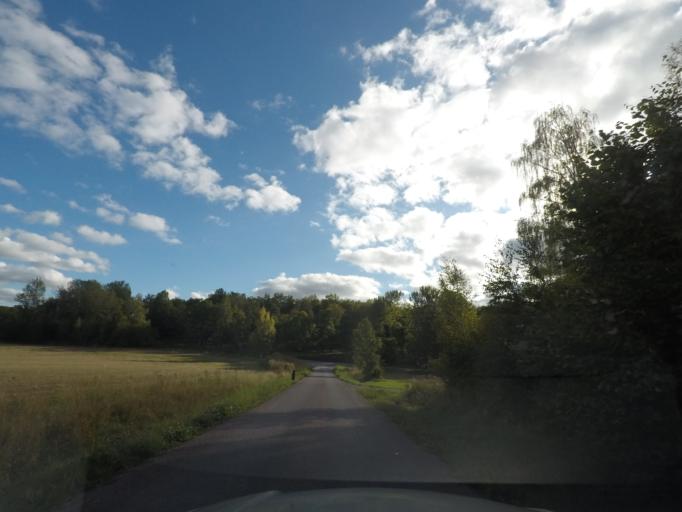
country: SE
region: Vaestmanland
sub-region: Kungsors Kommun
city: Kungsoer
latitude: 59.4847
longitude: 16.1815
